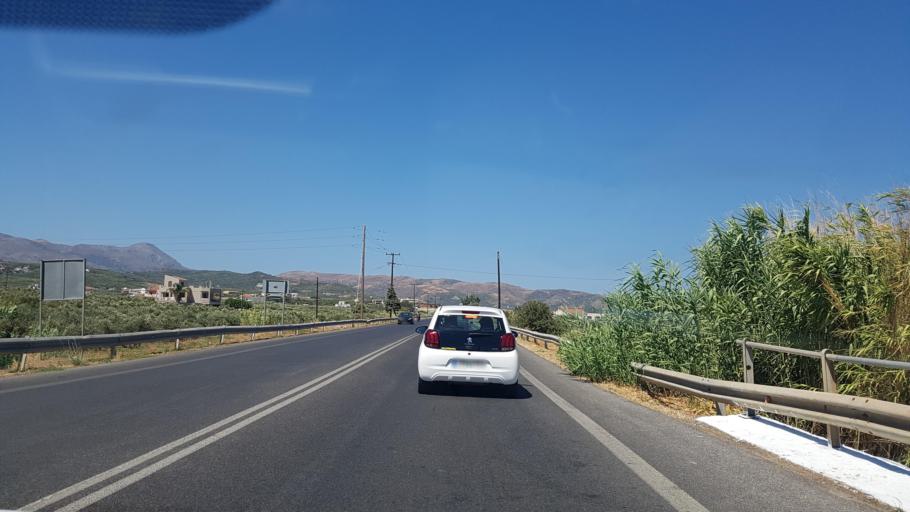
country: GR
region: Crete
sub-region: Nomos Chanias
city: Kissamos
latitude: 35.4973
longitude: 23.6962
